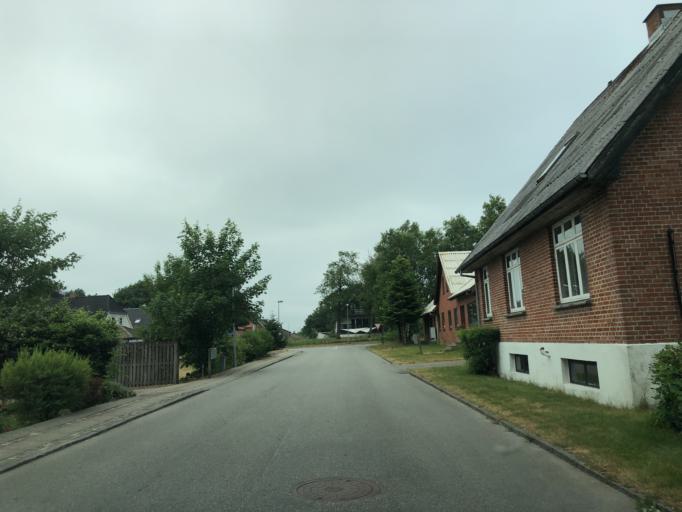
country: DK
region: Central Jutland
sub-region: Holstebro Kommune
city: Holstebro
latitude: 56.2561
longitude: 8.5646
